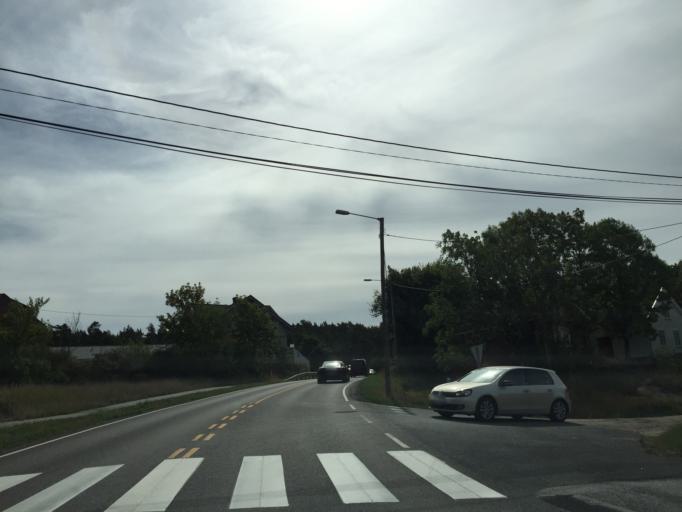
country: NO
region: Ostfold
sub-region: Fredrikstad
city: Fredrikstad
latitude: 59.1608
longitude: 10.9309
